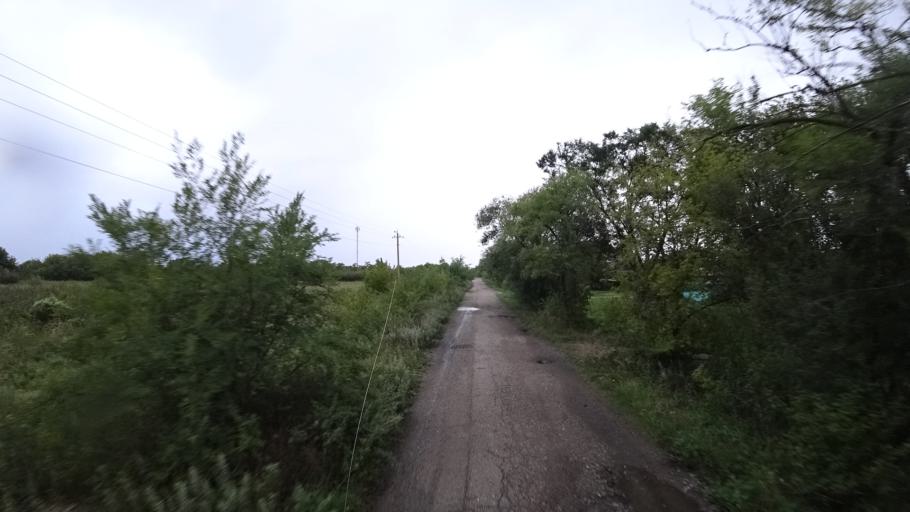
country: RU
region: Primorskiy
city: Chernigovka
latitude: 44.4006
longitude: 132.5314
